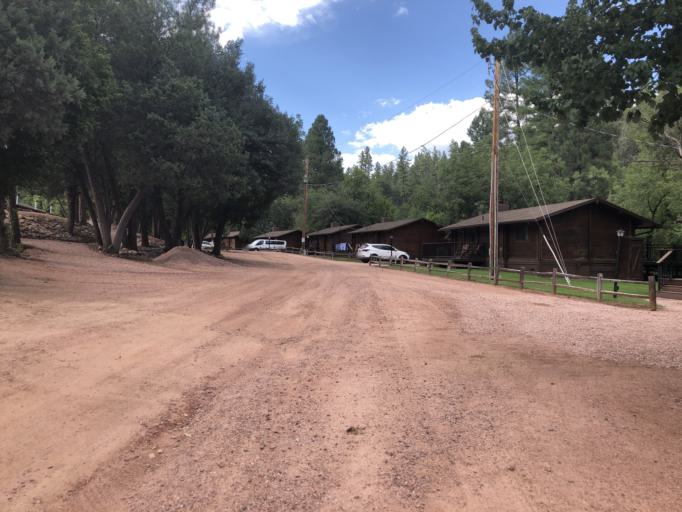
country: US
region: Arizona
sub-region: Gila County
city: Star Valley
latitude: 34.3246
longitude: -111.0933
